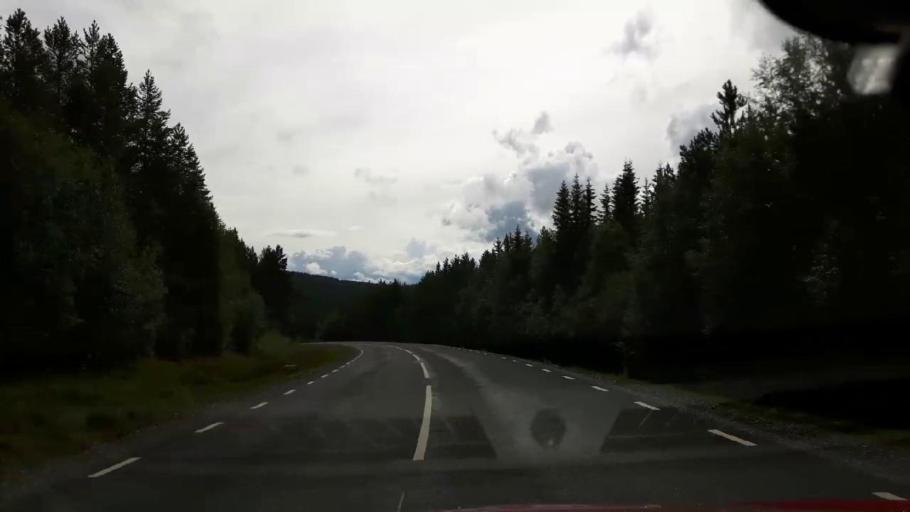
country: NO
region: Nord-Trondelag
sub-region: Lierne
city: Sandvika
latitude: 64.6382
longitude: 14.1368
